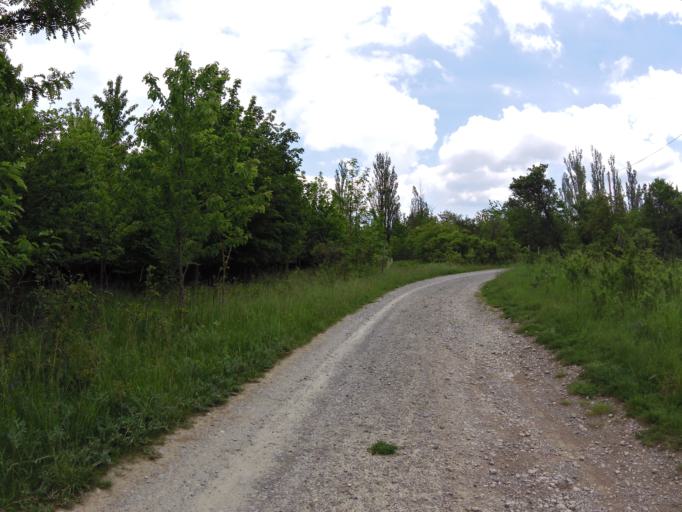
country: DE
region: Bavaria
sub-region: Regierungsbezirk Unterfranken
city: Winterhausen
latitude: 49.7168
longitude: 10.0188
